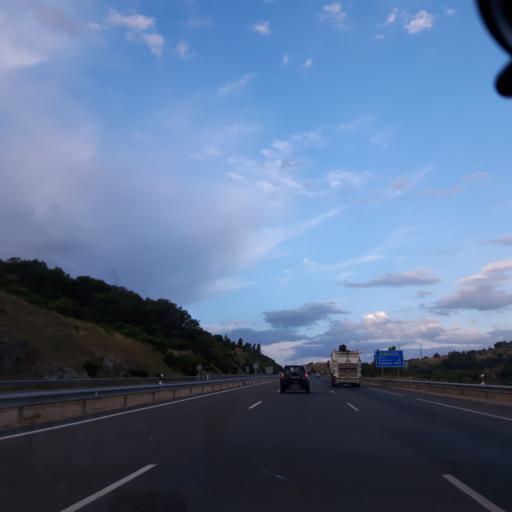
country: ES
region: Castille and Leon
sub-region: Provincia de Salamanca
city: Fresnedoso
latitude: 40.4288
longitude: -5.6986
